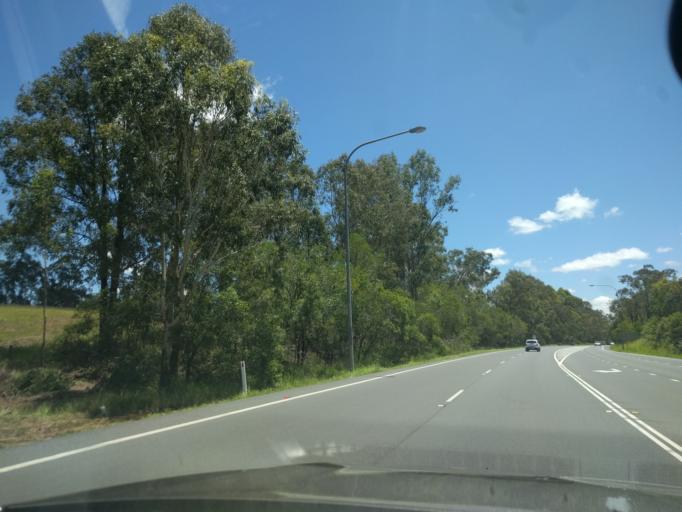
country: AU
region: Queensland
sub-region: Logan
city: Cedar Vale
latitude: -27.8634
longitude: 153.0002
